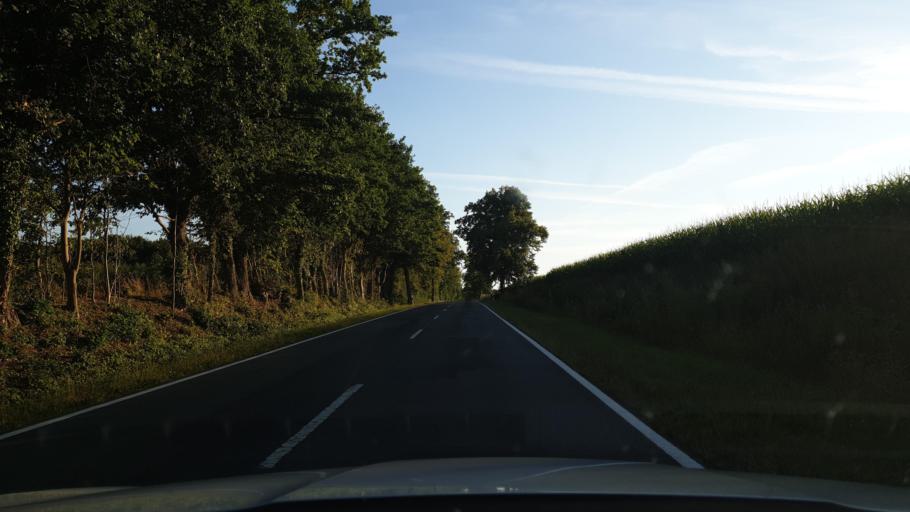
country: DE
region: Lower Saxony
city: Apelern
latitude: 52.2815
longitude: 9.3050
